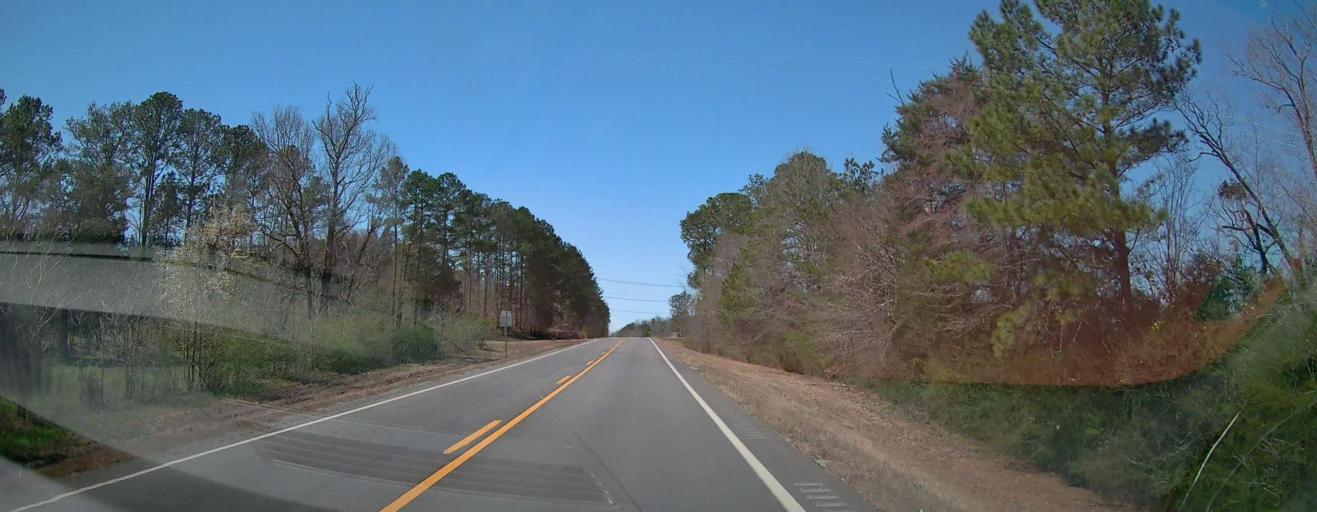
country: US
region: Alabama
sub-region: Calhoun County
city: Alexandria
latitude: 33.7845
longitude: -85.9362
